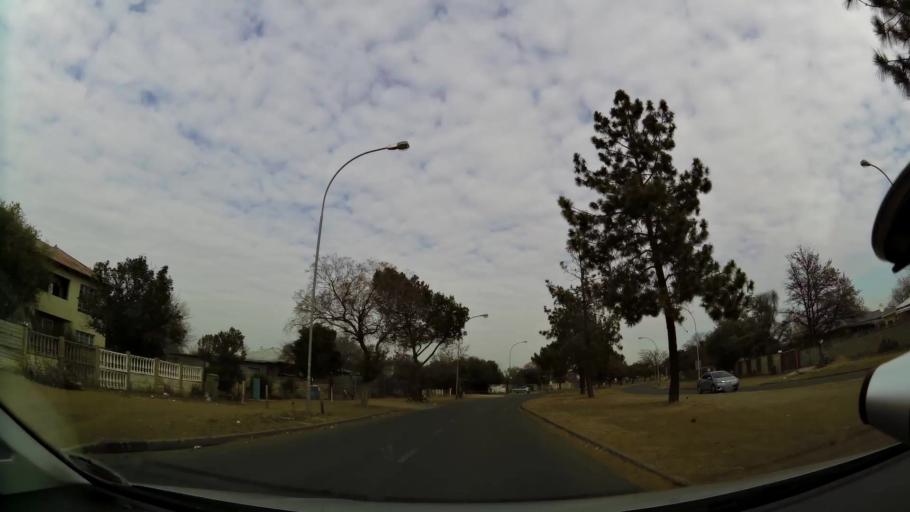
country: ZA
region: Orange Free State
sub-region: Mangaung Metropolitan Municipality
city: Bloemfontein
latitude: -29.1306
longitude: 26.1915
